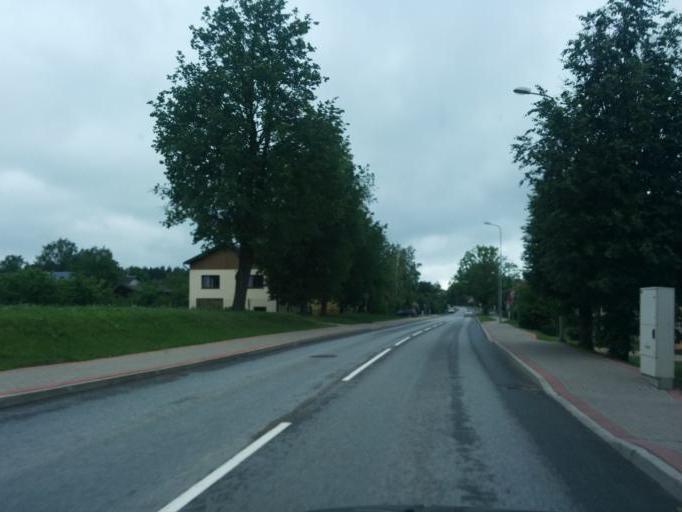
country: LV
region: Smiltene
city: Smiltene
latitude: 57.4285
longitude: 25.8916
